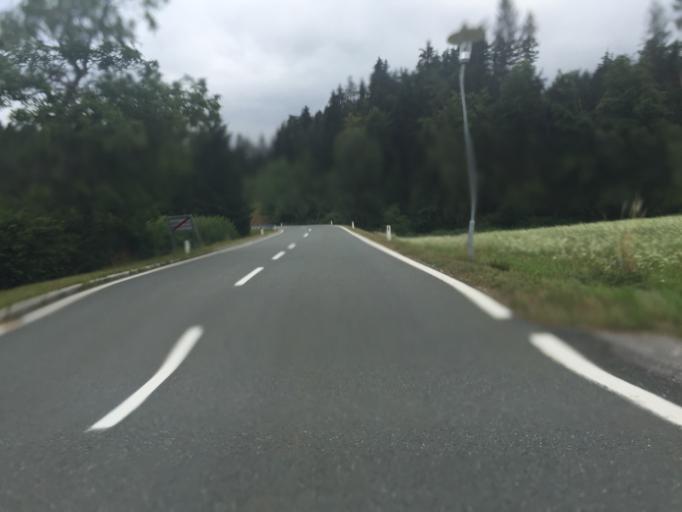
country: AT
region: Carinthia
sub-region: Politischer Bezirk Volkermarkt
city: Feistritz ob Bleiburg
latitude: 46.5534
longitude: 14.7675
